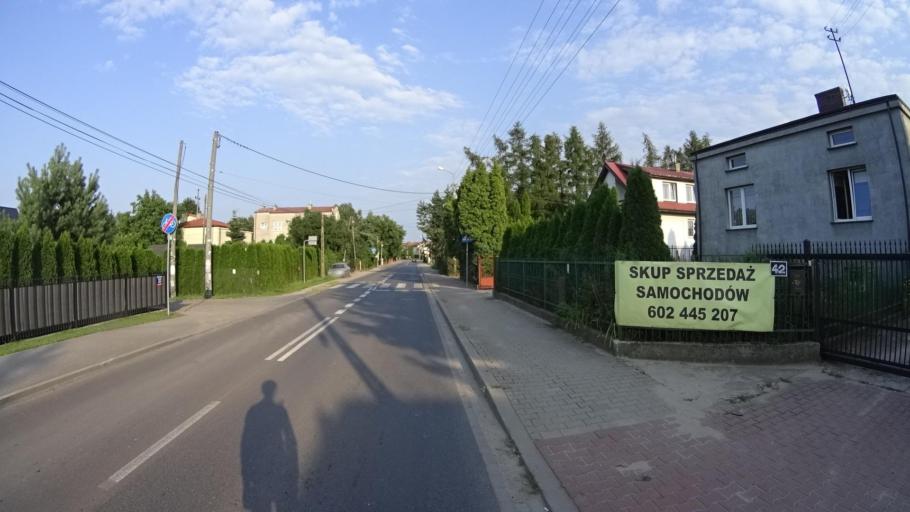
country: PL
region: Masovian Voivodeship
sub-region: Powiat pruszkowski
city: Rybie
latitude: 52.1463
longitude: 20.9475
